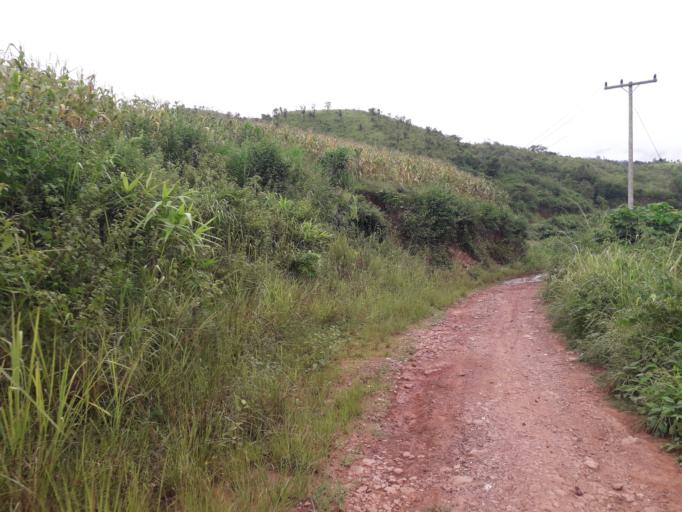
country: CN
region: Yunnan
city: Menglie
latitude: 22.2584
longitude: 101.5947
